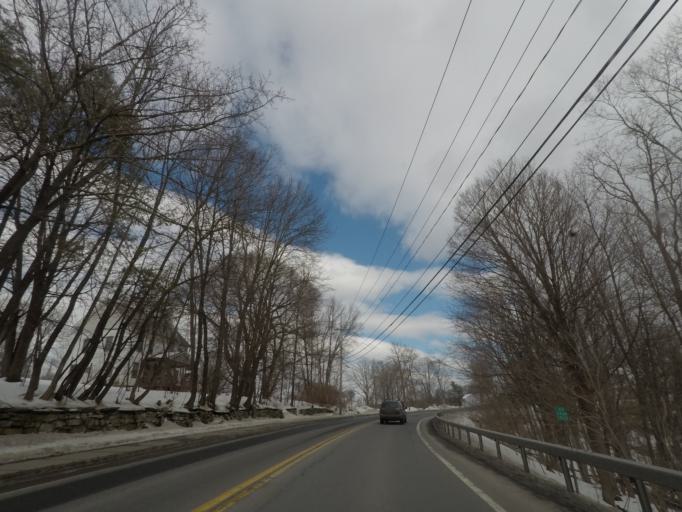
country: US
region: New York
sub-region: Washington County
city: Greenwich
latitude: 43.1032
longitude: -73.5232
